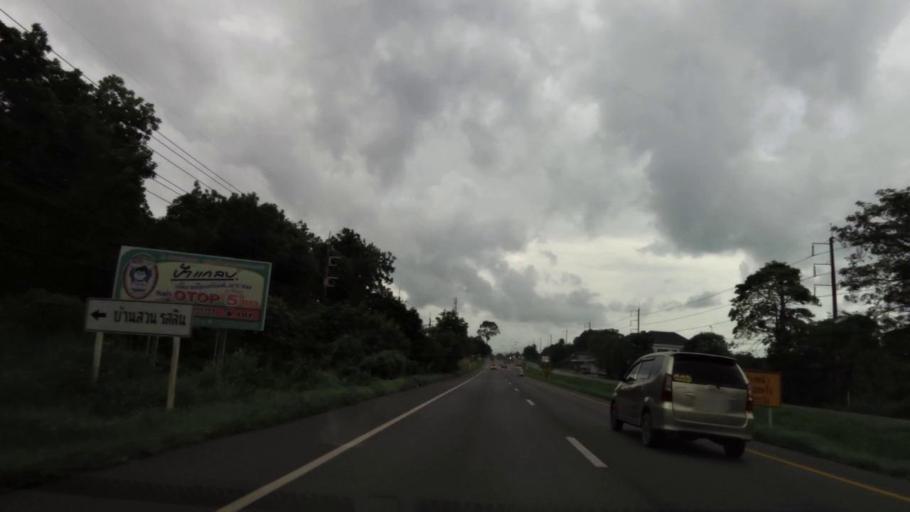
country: TH
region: Chanthaburi
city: Tha Mai
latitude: 12.6867
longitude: 102.0004
